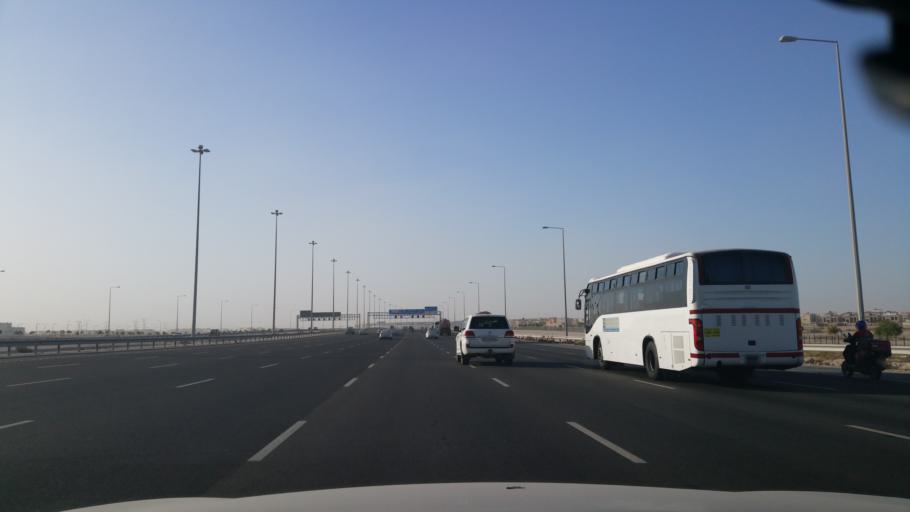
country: QA
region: Al Wakrah
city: Al Wukayr
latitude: 25.1705
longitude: 51.5594
